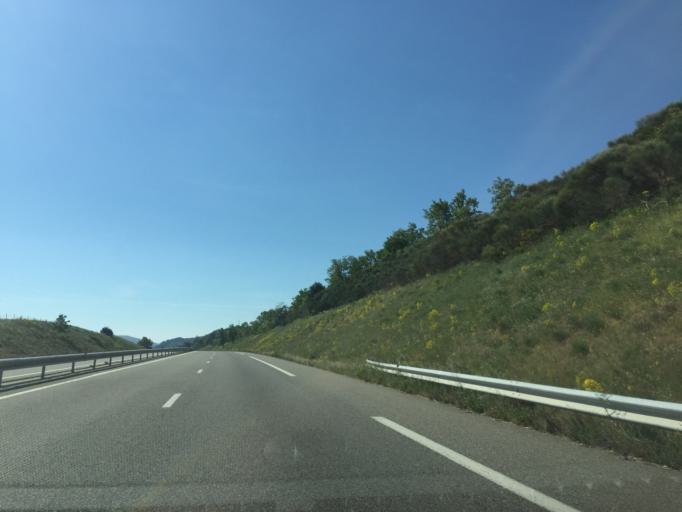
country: FR
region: Provence-Alpes-Cote d'Azur
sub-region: Departement des Alpes-de-Haute-Provence
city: Volonne
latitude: 44.1147
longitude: 5.9857
